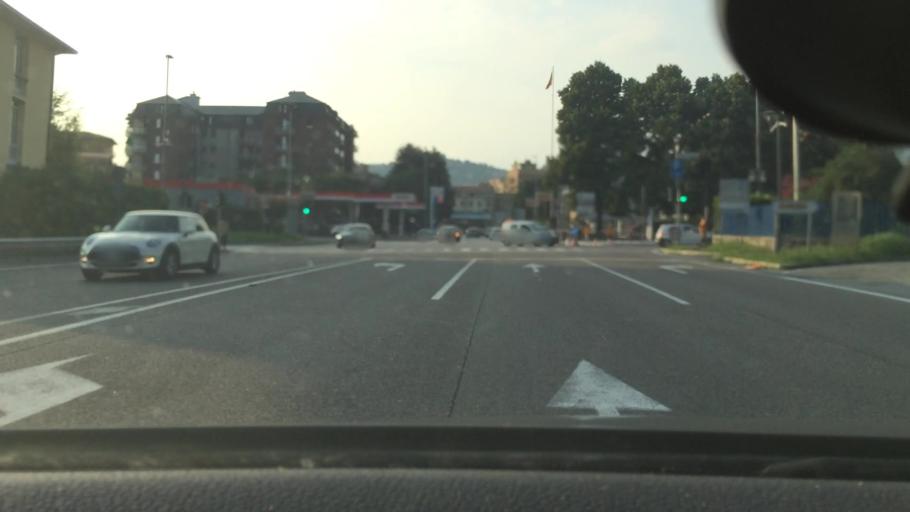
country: IT
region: Lombardy
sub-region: Provincia di Bergamo
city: Bergamo
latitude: 45.6855
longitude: 9.6691
